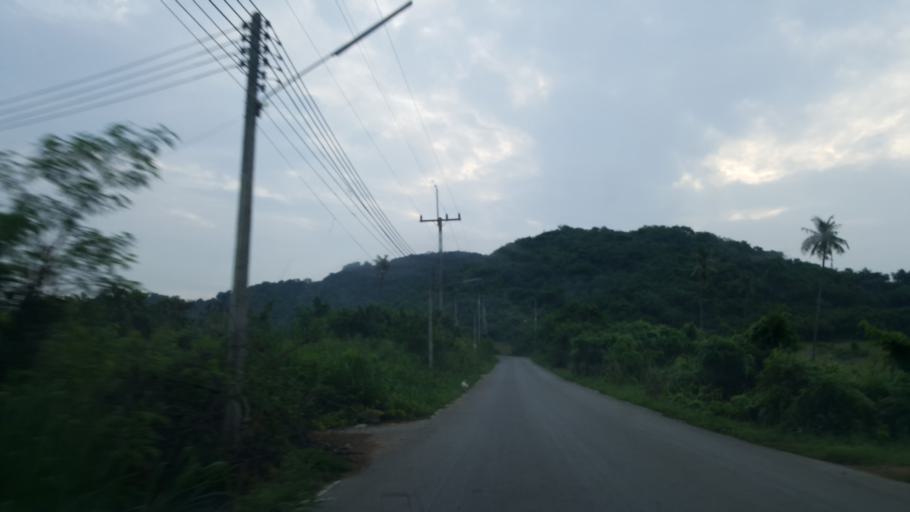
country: TH
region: Chon Buri
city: Sattahip
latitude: 12.7031
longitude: 100.9037
